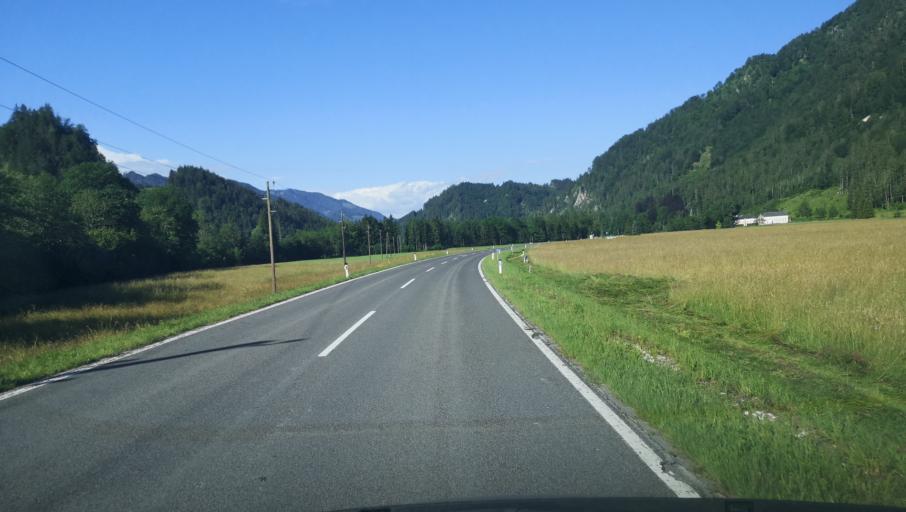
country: AT
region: Lower Austria
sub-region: Politischer Bezirk Amstetten
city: Opponitz
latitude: 47.8762
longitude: 14.8076
